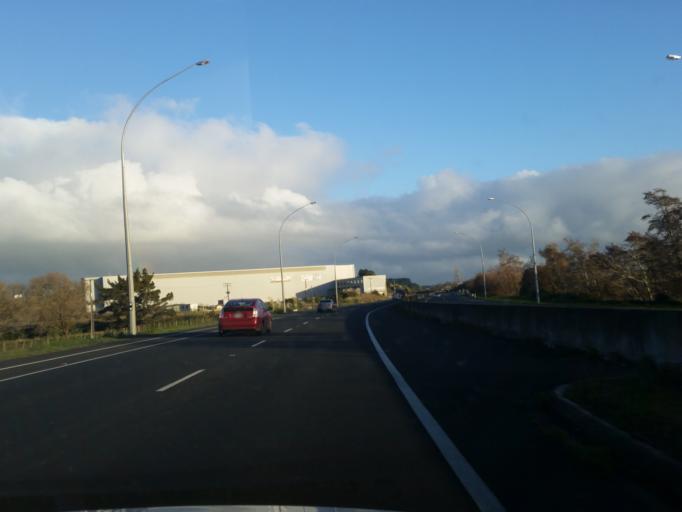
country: NZ
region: Waikato
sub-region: Waikato District
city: Te Kauwhata
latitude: -37.3099
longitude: 175.0674
